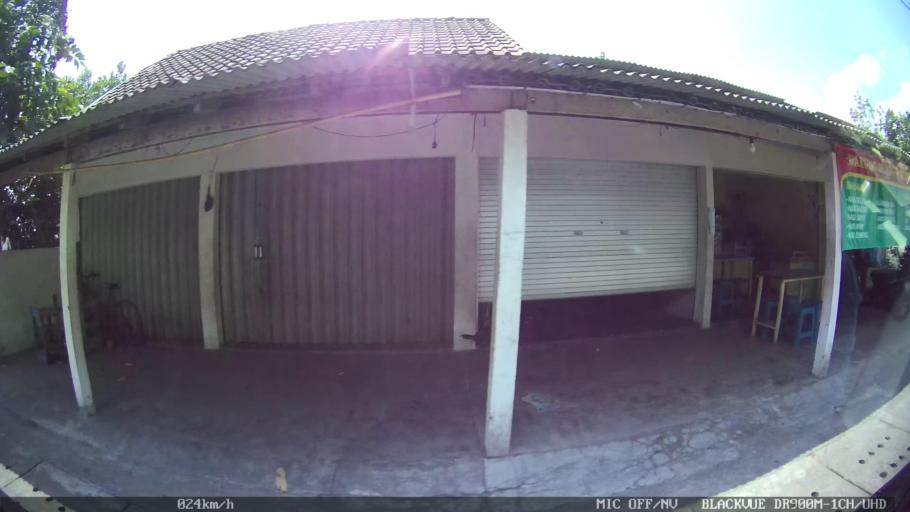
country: ID
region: Daerah Istimewa Yogyakarta
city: Yogyakarta
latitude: -7.8243
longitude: 110.4066
